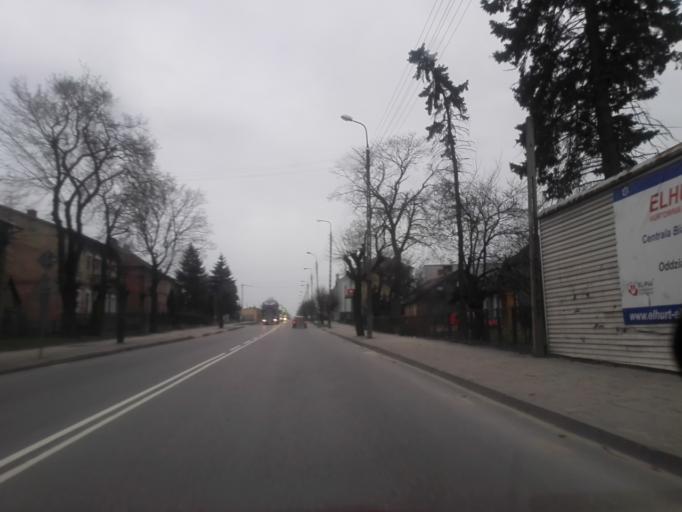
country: PL
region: Podlasie
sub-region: Powiat grajewski
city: Grajewo
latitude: 53.6456
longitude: 22.4516
